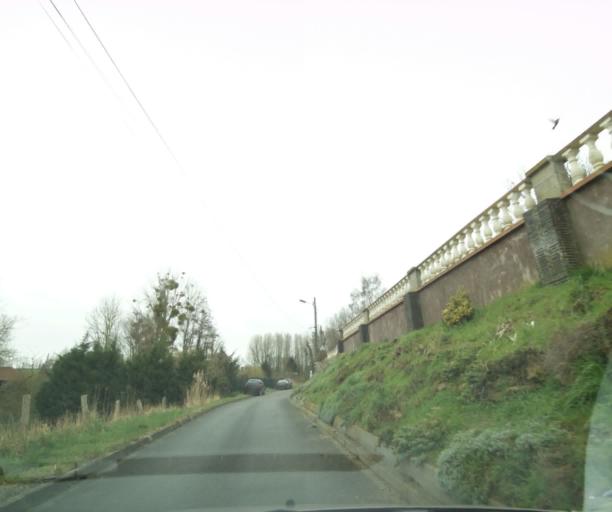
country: FR
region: Picardie
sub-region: Departement de l'Oise
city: Crisolles
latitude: 49.6010
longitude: 3.0201
